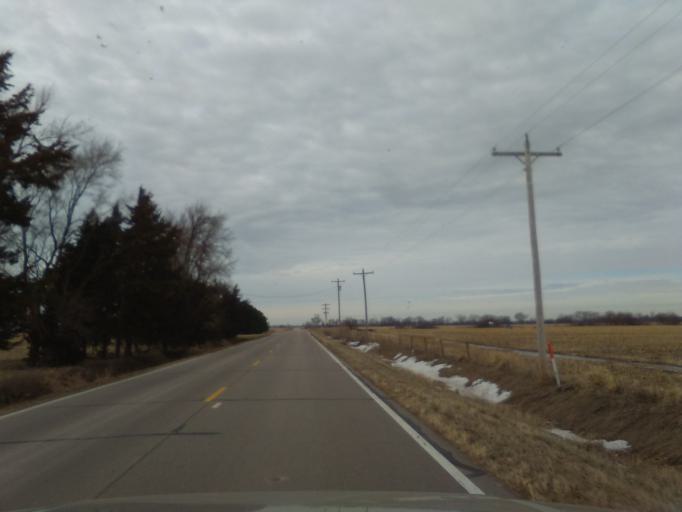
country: US
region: Nebraska
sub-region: Hall County
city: Grand Island
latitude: 40.7710
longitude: -98.4219
